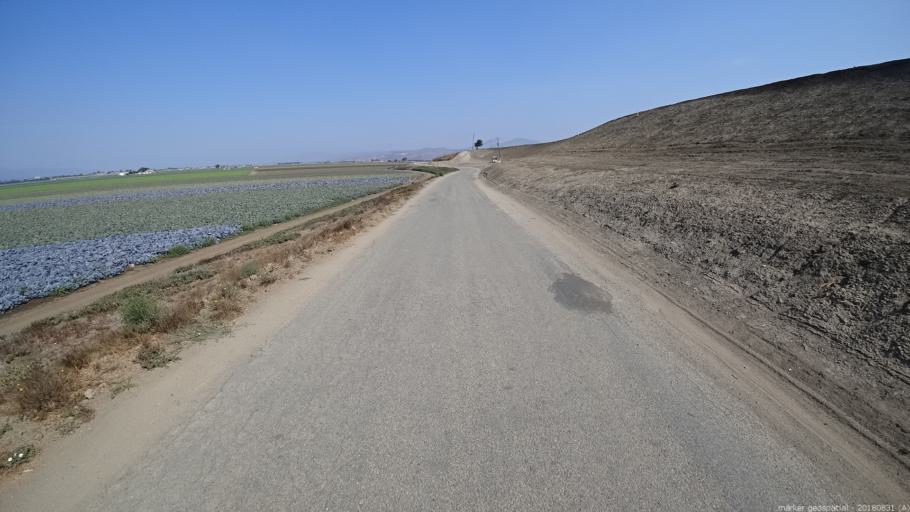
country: US
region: California
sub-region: Monterey County
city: Greenfield
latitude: 36.3032
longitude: -121.2053
